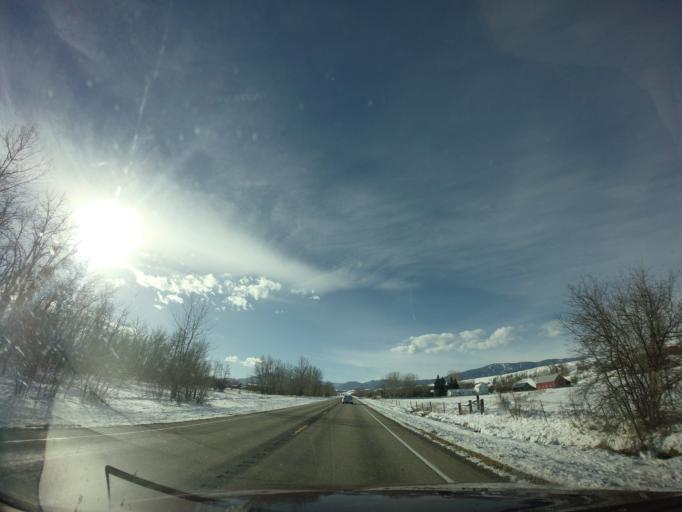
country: US
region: Montana
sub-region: Carbon County
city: Red Lodge
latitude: 45.2524
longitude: -109.2322
